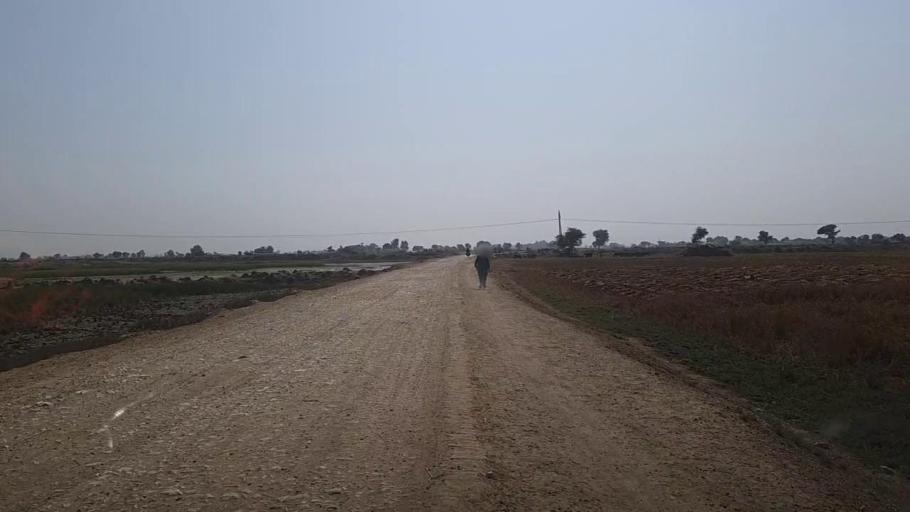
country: PK
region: Sindh
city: Kandhkot
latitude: 28.3901
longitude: 69.2934
